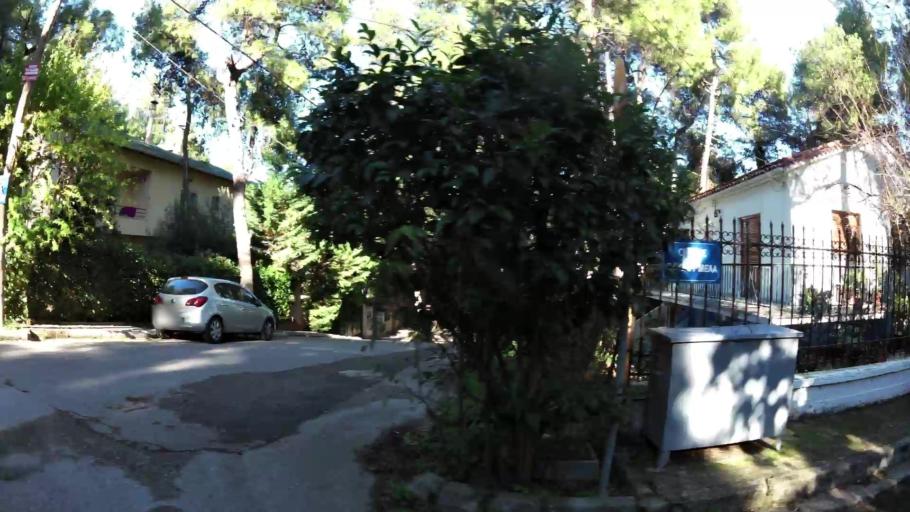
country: GR
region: Attica
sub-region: Nomarchia Anatolikis Attikis
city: Drosia
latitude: 38.1098
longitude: 23.8619
